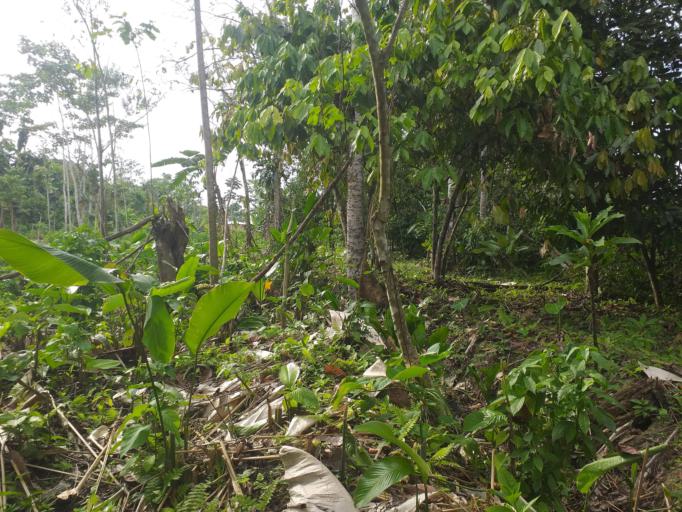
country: CO
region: Narino
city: La Tola
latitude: 2.3390
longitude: -78.3234
